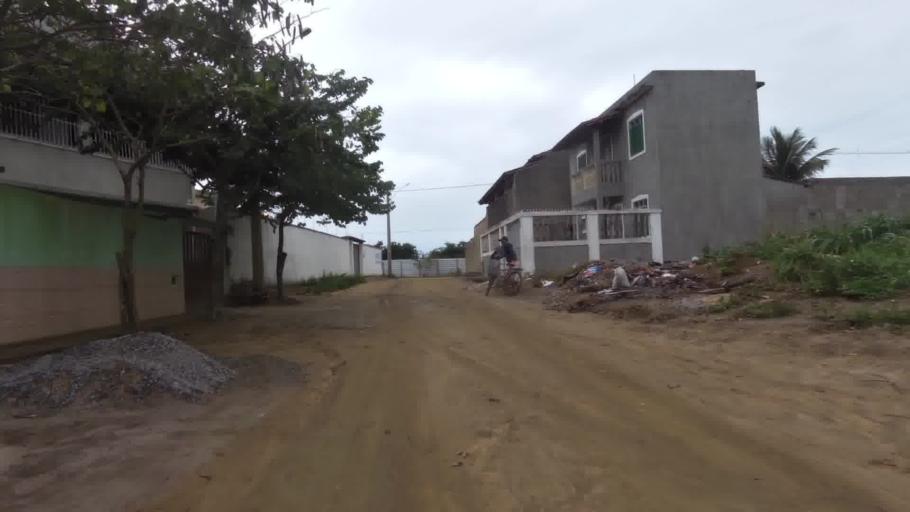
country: BR
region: Espirito Santo
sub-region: Marataizes
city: Marataizes
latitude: -21.0490
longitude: -40.8343
